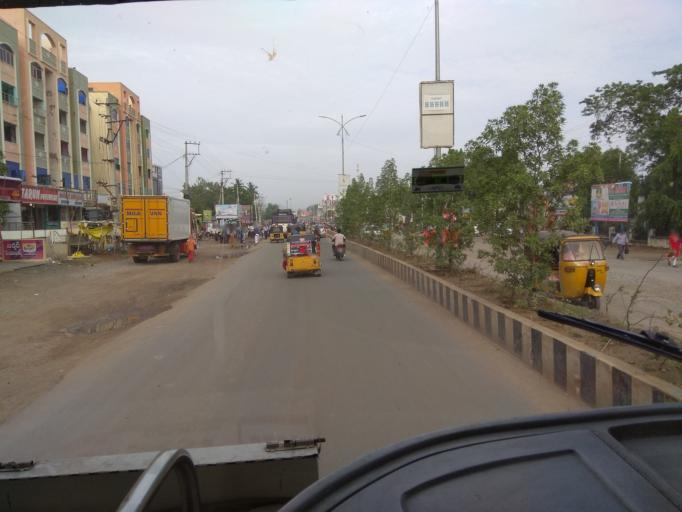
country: IN
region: Andhra Pradesh
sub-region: Guntur
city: Guntur
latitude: 16.2921
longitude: 80.4305
